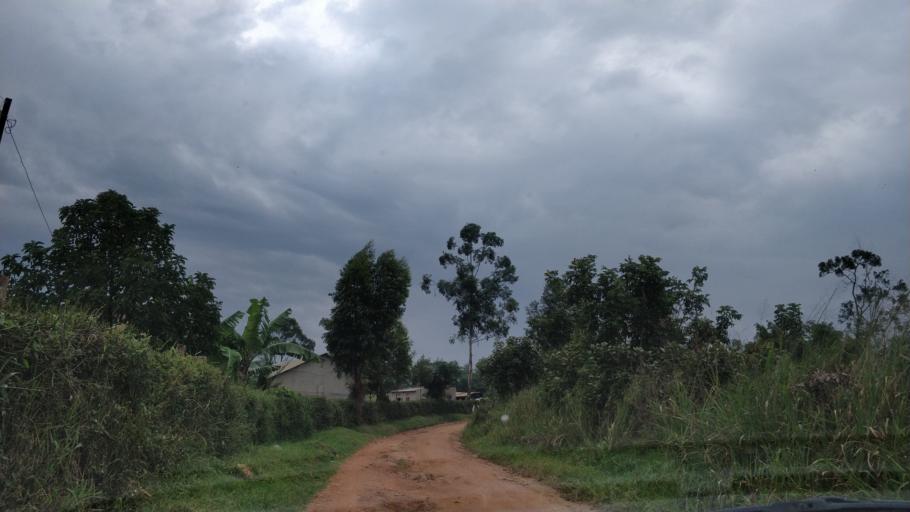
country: UG
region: Western Region
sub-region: Sheema District
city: Kibingo
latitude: -0.6444
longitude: 30.4960
